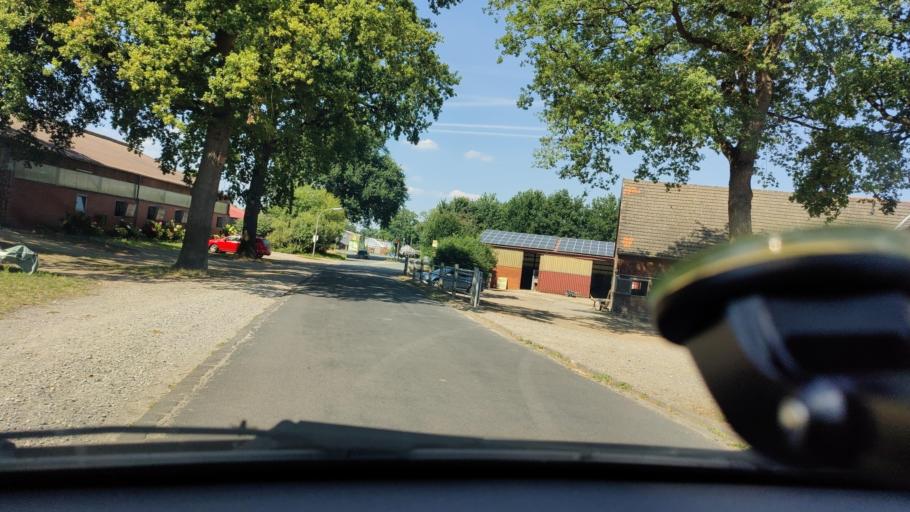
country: DE
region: North Rhine-Westphalia
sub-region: Regierungsbezirk Dusseldorf
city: Schermbeck
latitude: 51.6562
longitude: 6.9041
